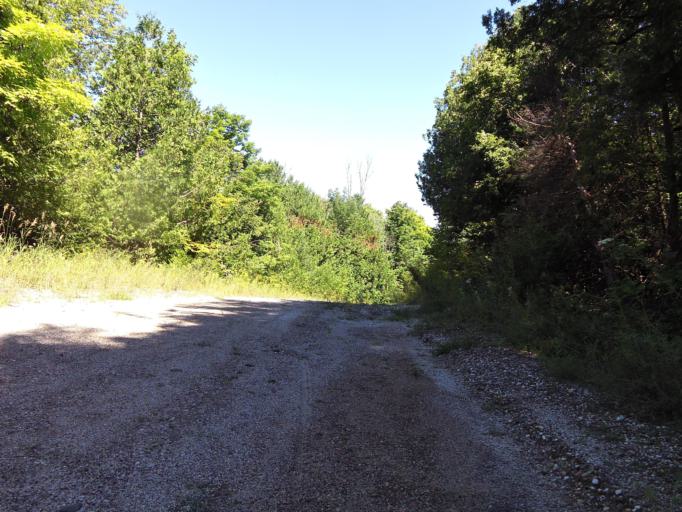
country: CA
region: Ontario
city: Arnprior
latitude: 45.1603
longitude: -76.4920
